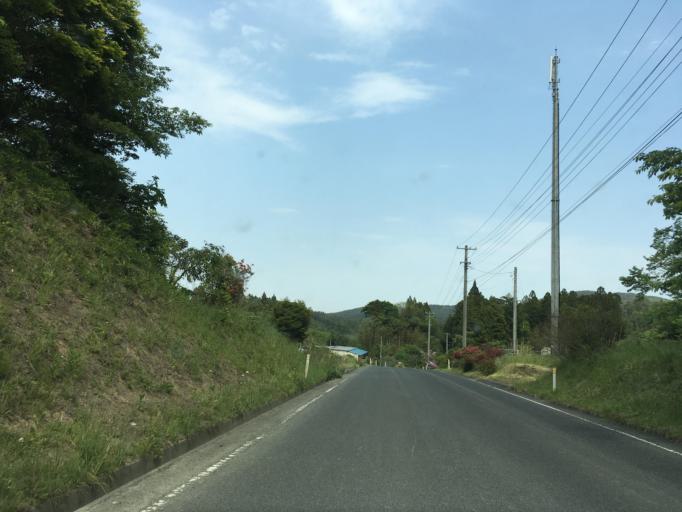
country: JP
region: Iwate
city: Ofunato
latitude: 38.8552
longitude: 141.5139
